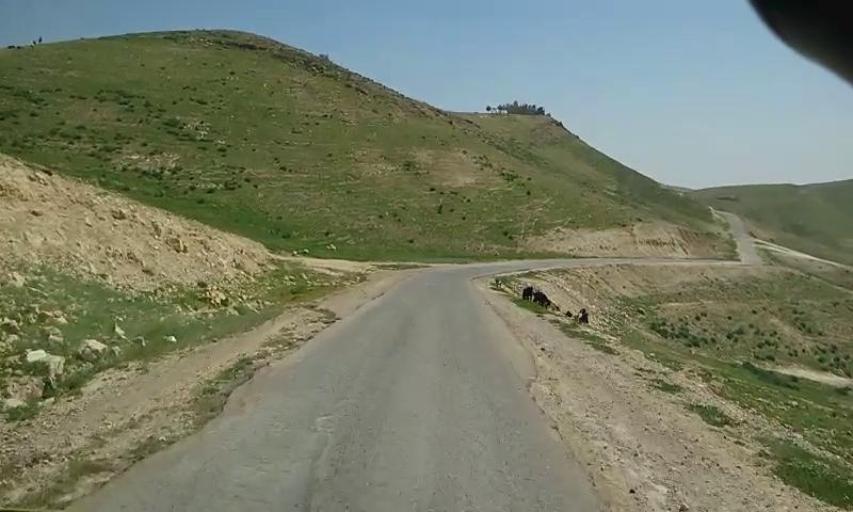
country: PS
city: `Arab ar Rashaydah
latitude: 31.5648
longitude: 35.2400
